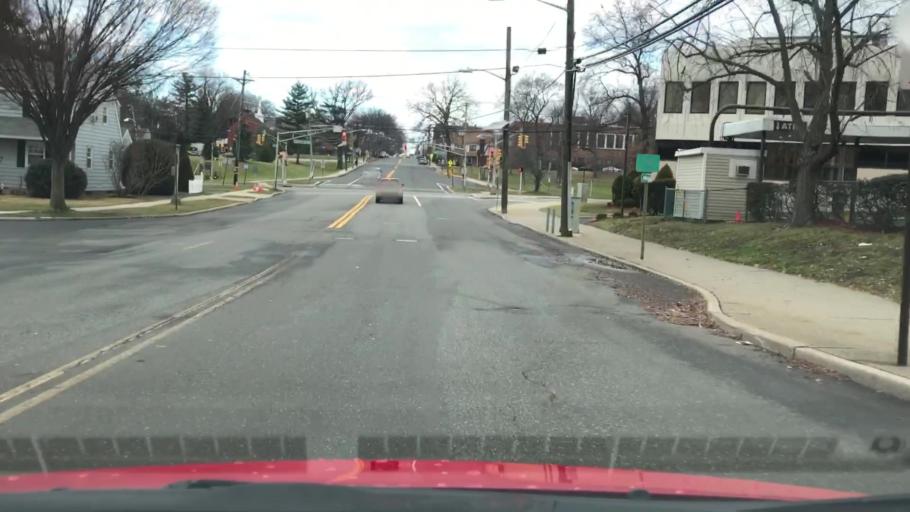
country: US
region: New Jersey
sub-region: Bergen County
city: Teaneck
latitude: 40.8840
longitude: -74.0062
